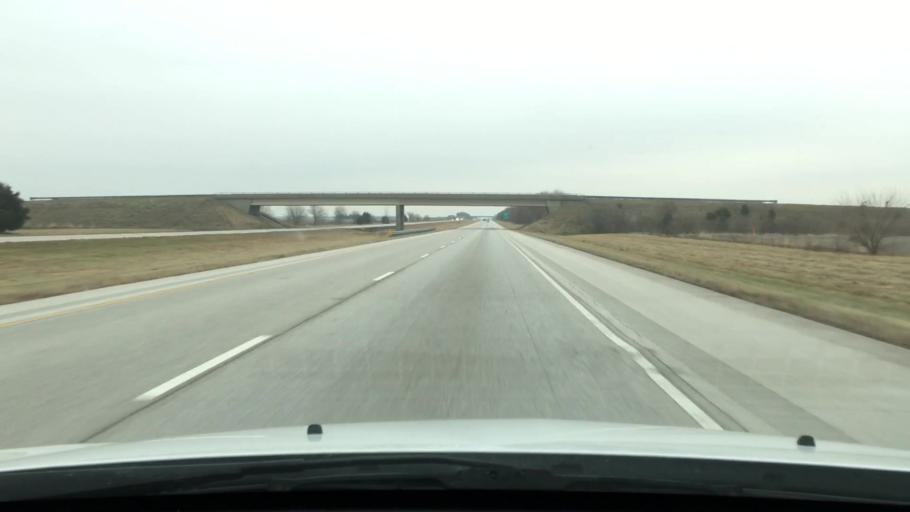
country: US
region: Illinois
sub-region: Scott County
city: Winchester
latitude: 39.6801
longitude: -90.3491
